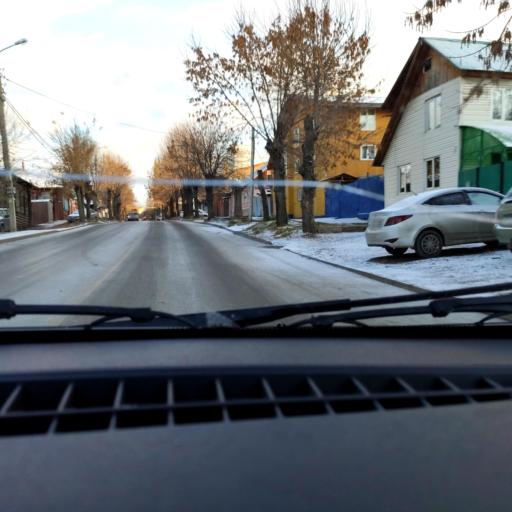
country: RU
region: Bashkortostan
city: Ufa
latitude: 54.7234
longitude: 55.9687
